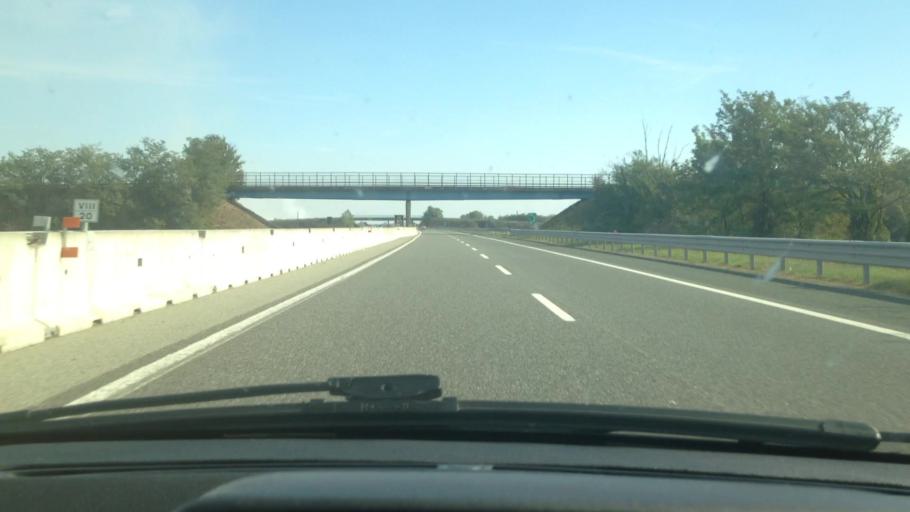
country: IT
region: Piedmont
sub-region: Provincia di Vercelli
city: Crova
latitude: 45.3275
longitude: 8.2355
